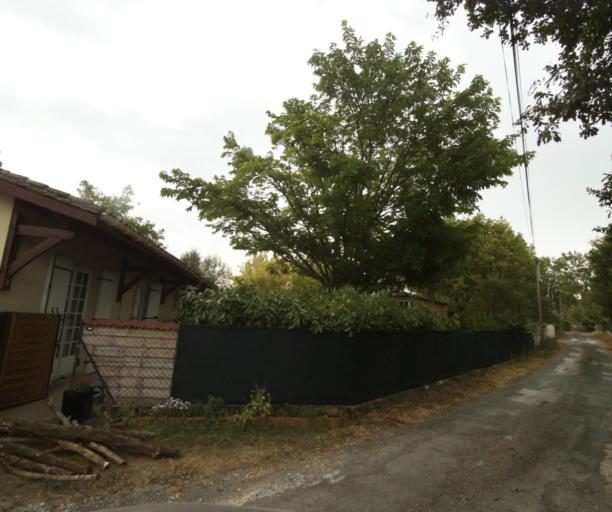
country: FR
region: Aquitaine
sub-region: Departement de la Gironde
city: La Sauve
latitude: 44.7507
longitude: -0.3347
